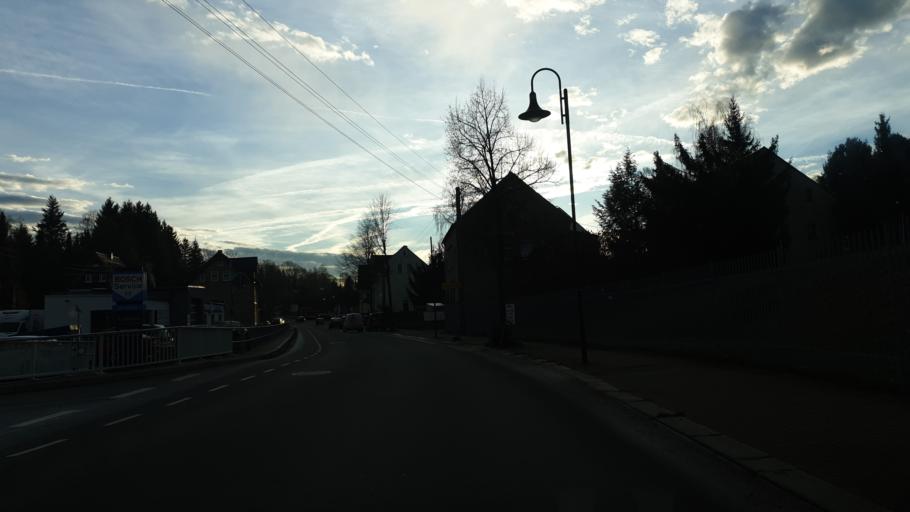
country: DE
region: Saxony
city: Kirchberg
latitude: 50.7918
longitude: 12.7591
